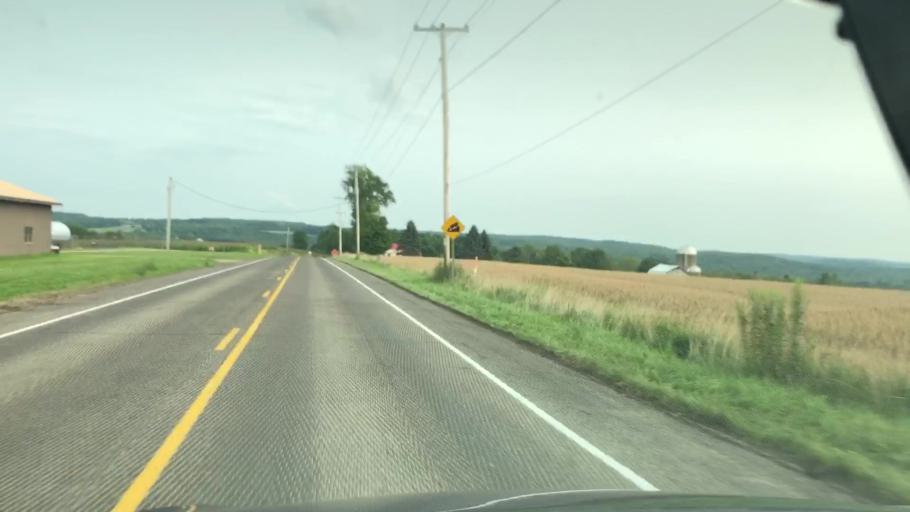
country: US
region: Pennsylvania
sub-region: Crawford County
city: Titusville
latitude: 41.7473
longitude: -79.7684
